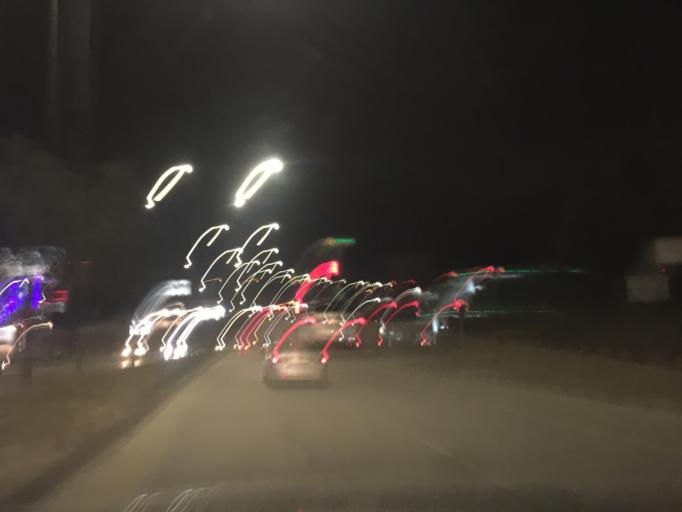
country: JO
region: Amman
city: Umm as Summaq
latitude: 31.8805
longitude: 35.8428
